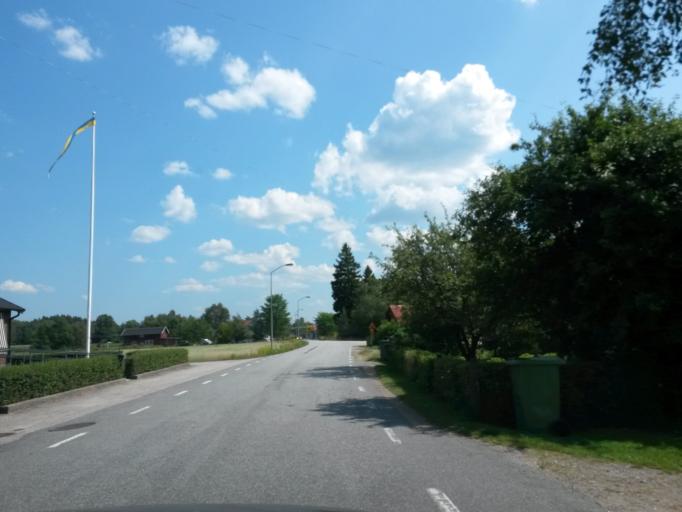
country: SE
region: Vaestra Goetaland
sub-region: Herrljunga Kommun
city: Herrljunga
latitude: 58.0854
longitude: 13.0251
